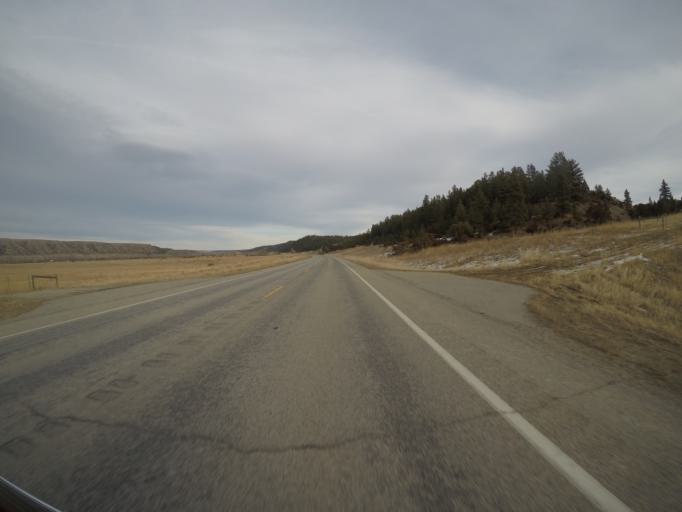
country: US
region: Montana
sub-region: Stillwater County
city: Absarokee
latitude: 45.5452
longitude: -109.3784
